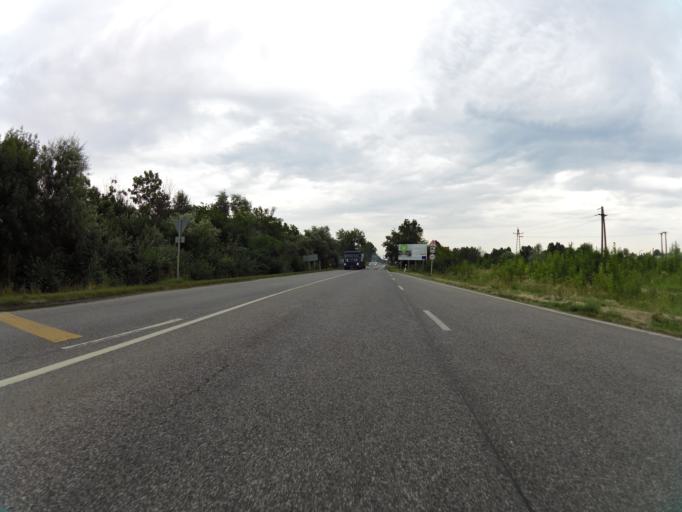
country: HU
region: Csongrad
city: Szeged
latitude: 46.2816
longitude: 20.0933
